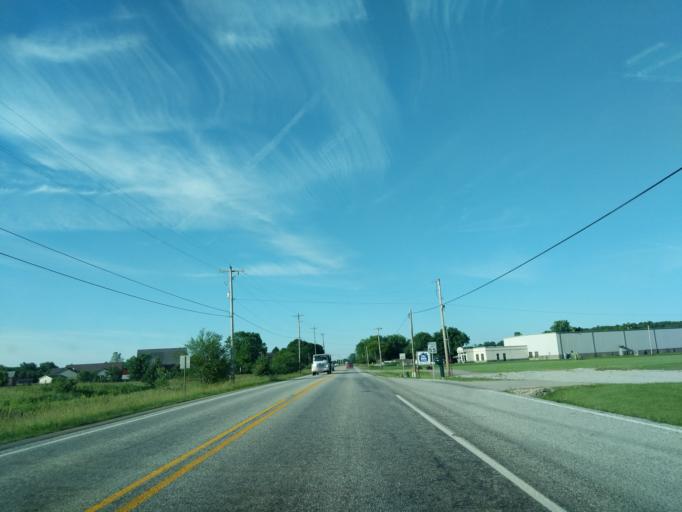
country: US
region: Indiana
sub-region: Madison County
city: Pendleton
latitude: 39.9804
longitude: -85.7533
